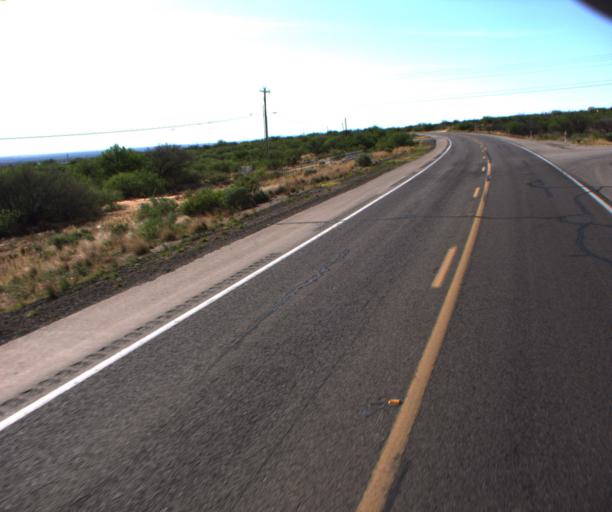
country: US
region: Arizona
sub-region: Cochise County
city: Benson
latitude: 31.9351
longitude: -110.2855
